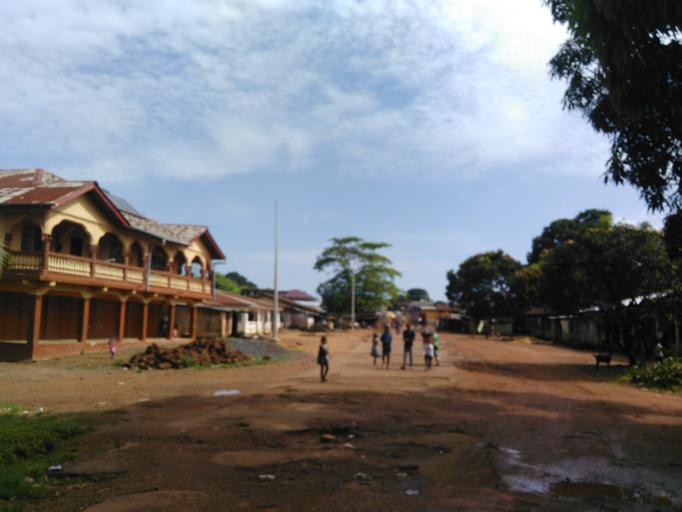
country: SL
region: Southern Province
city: Rotifunk
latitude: 8.4877
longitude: -12.7583
